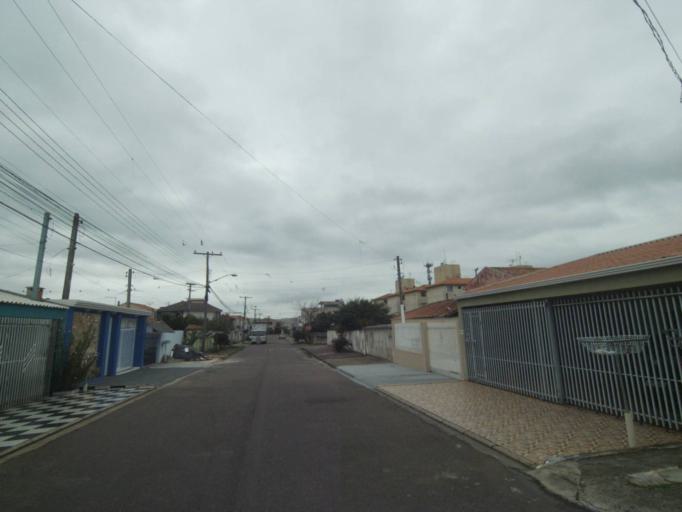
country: BR
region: Parana
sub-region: Sao Jose Dos Pinhais
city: Sao Jose dos Pinhais
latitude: -25.5429
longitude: -49.2557
